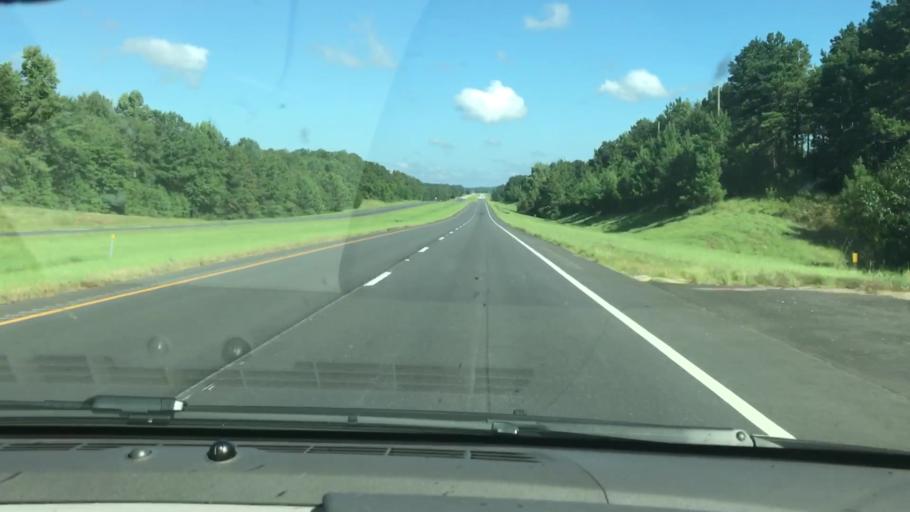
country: US
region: Alabama
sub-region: Barbour County
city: Eufaula
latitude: 32.0525
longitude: -85.1345
